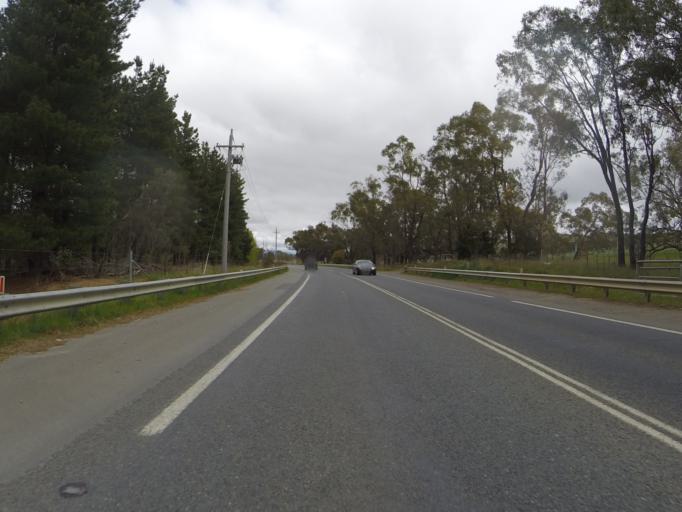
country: AU
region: Australian Capital Territory
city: Canberra
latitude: -35.2458
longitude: 149.1915
